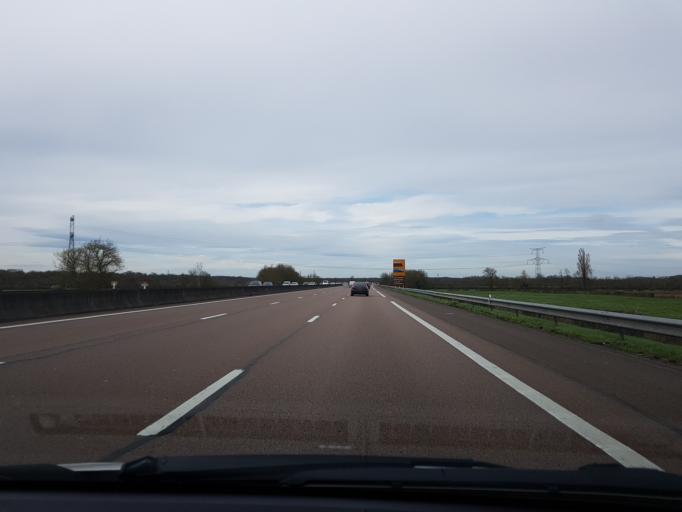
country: FR
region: Bourgogne
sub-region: Departement de Saone-et-Loire
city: Sennecey-le-Grand
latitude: 46.6643
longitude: 4.8525
